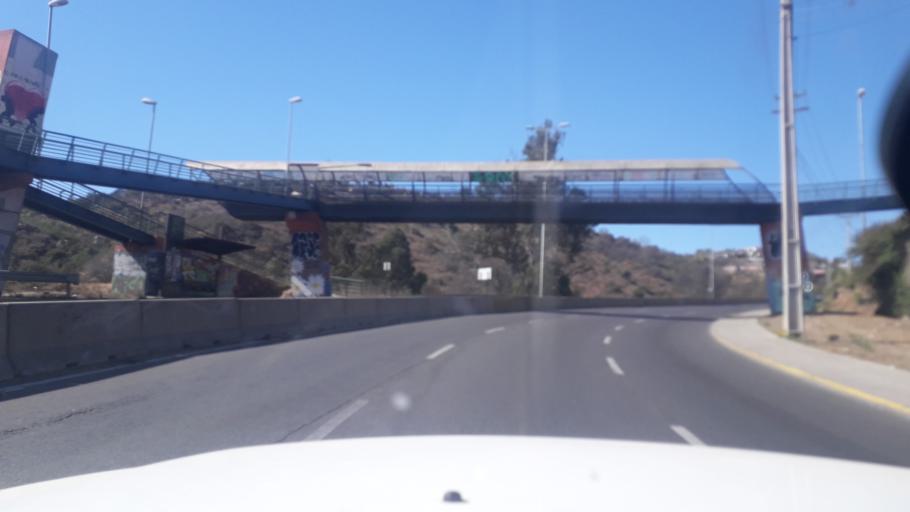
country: CL
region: Valparaiso
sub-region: Provincia de Valparaiso
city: Vina del Mar
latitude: -33.0348
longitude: -71.5156
